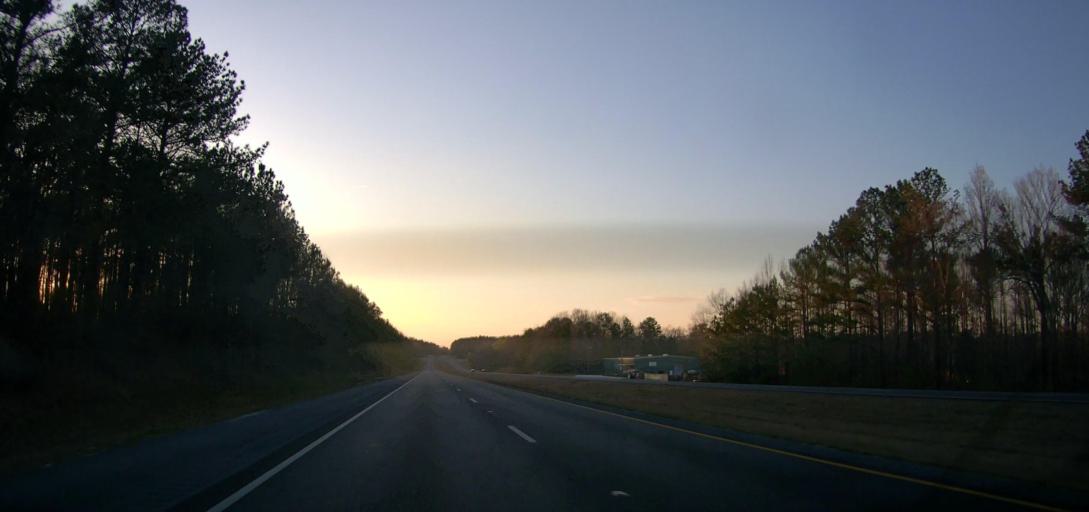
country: US
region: Alabama
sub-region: Coosa County
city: Stewartville
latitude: 33.0888
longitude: -86.2056
